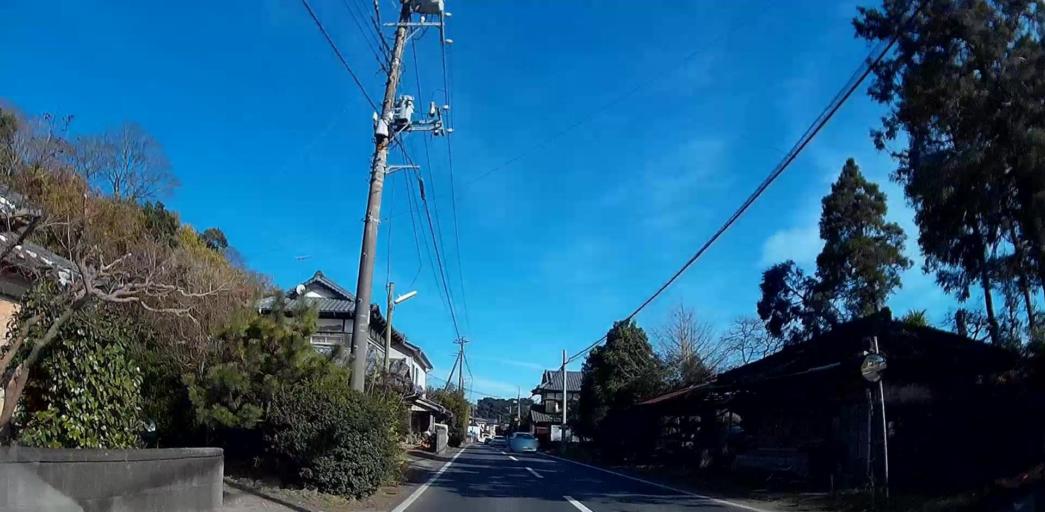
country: JP
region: Chiba
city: Yokaichiba
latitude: 35.7361
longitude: 140.4977
